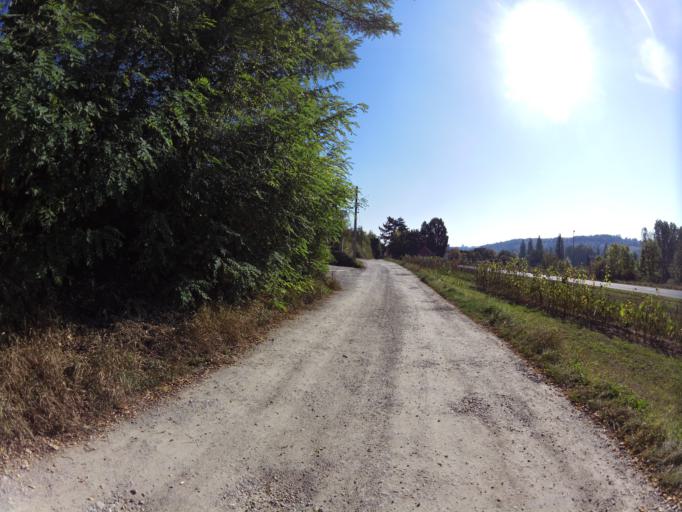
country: DE
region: Bavaria
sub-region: Regierungsbezirk Unterfranken
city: Ochsenfurt
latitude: 49.6758
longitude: 10.0462
